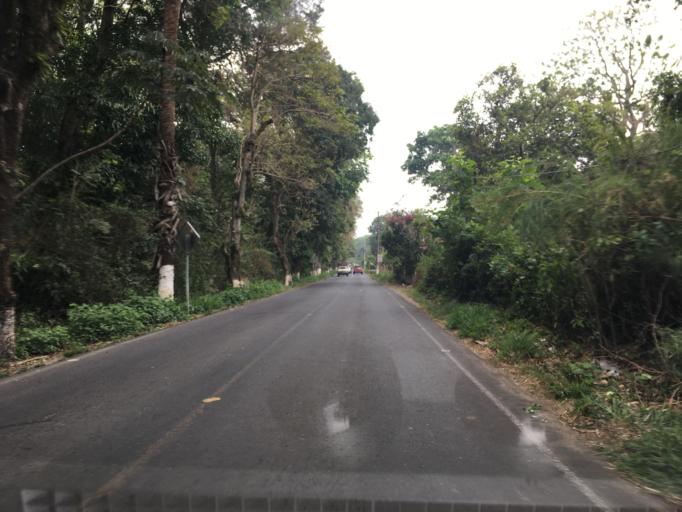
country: GT
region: Guatemala
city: Fraijanes
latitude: 14.3975
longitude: -90.4758
